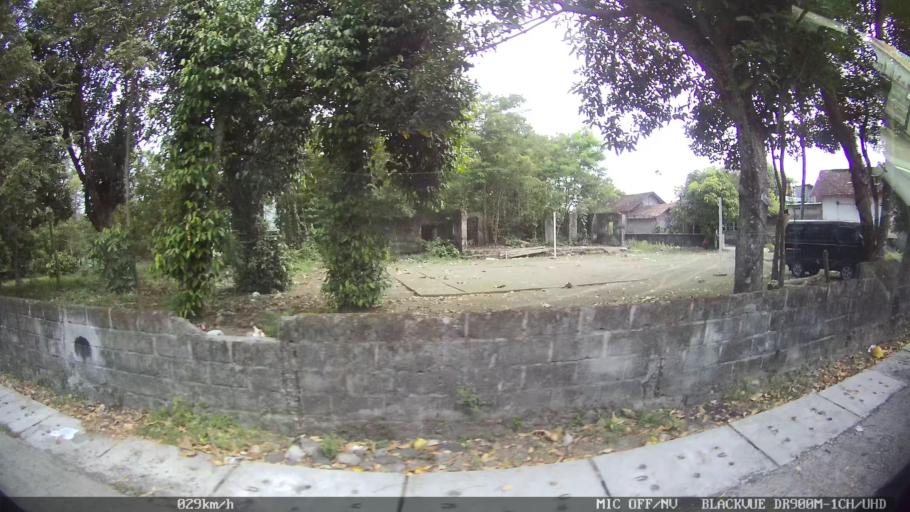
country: ID
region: Daerah Istimewa Yogyakarta
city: Depok
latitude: -7.7301
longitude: 110.4522
